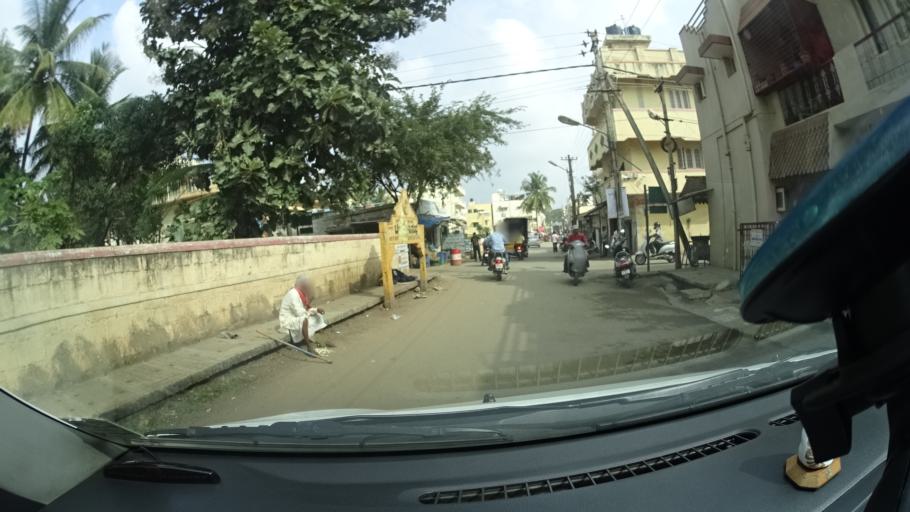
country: IN
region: Karnataka
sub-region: Bangalore Urban
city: Yelahanka
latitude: 13.0906
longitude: 77.5812
